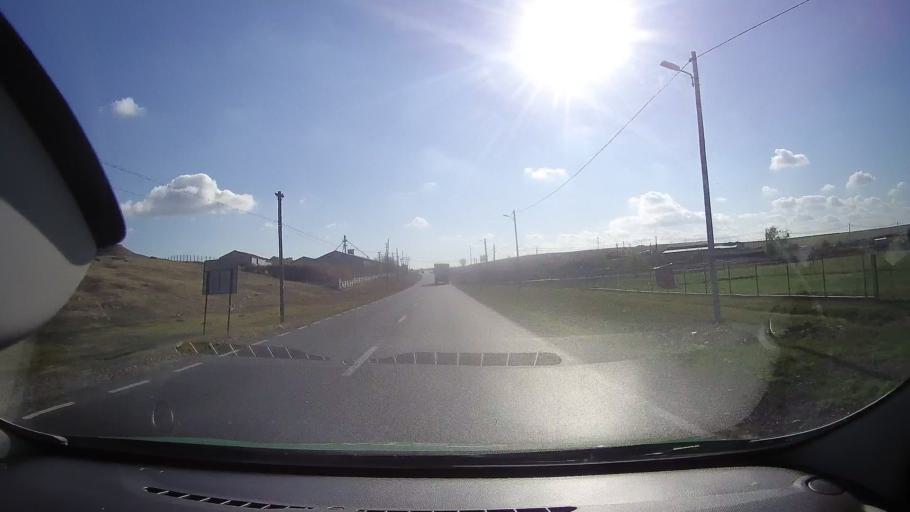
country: RO
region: Tulcea
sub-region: Comuna Baia
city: Baia
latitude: 44.7190
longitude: 28.6802
